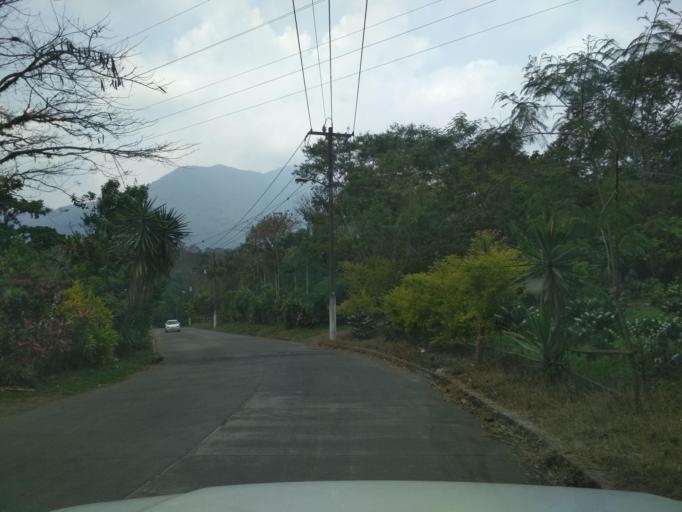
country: MX
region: Veracruz
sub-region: Cordoba
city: San Jose de Tapia
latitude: 18.8362
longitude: -96.9812
